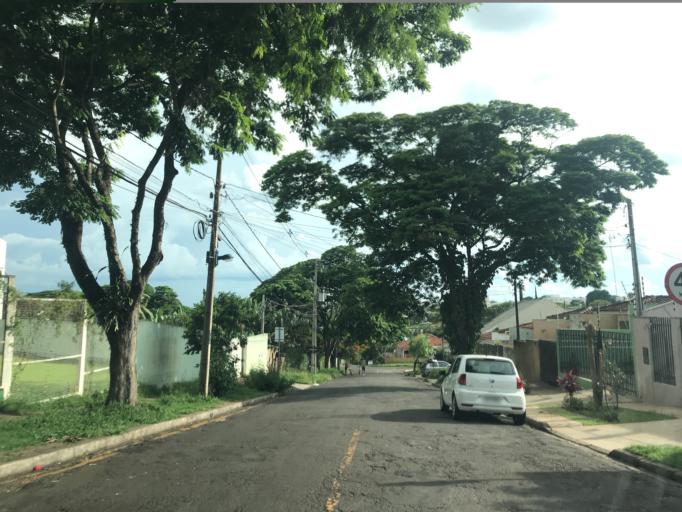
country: BR
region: Parana
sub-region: Maringa
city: Maringa
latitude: -23.4370
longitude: -51.9498
